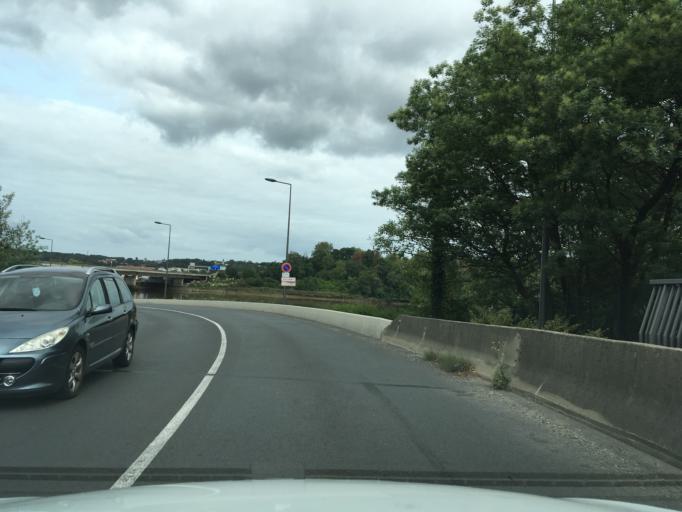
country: FR
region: Aquitaine
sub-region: Departement des Pyrenees-Atlantiques
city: Mouguerre
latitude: 43.4836
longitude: -1.4452
